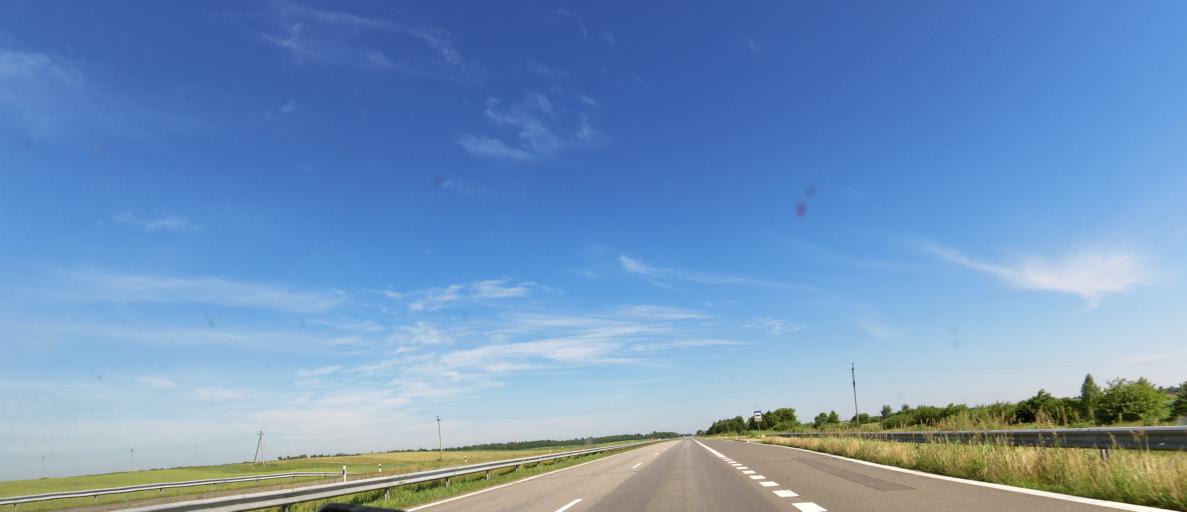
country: LT
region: Vilnius County
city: Ukmerge
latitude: 55.1592
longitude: 24.8199
